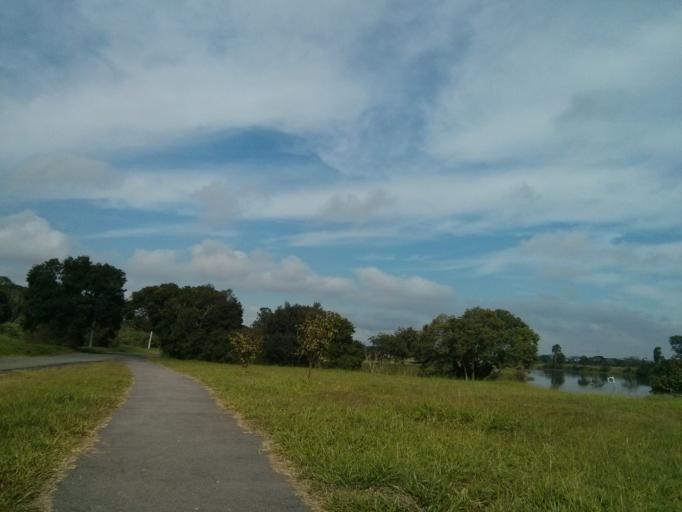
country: BR
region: Parana
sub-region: Sao Jose Dos Pinhais
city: Sao Jose dos Pinhais
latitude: -25.5133
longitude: -49.2143
